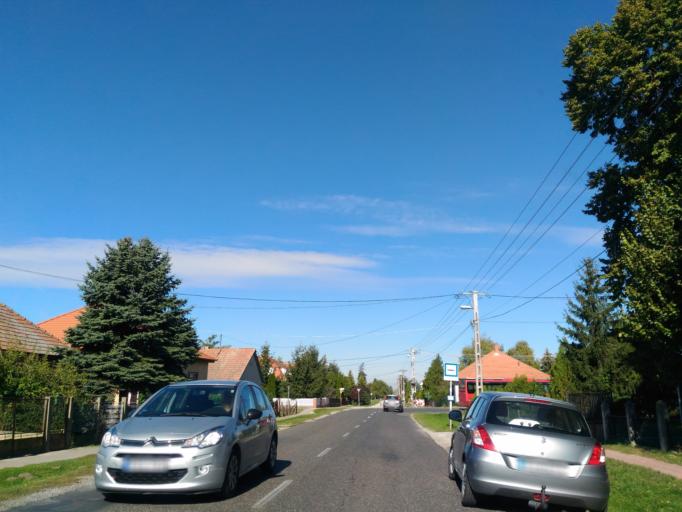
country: HU
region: Fejer
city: Ivancsa
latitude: 47.1546
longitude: 18.8227
